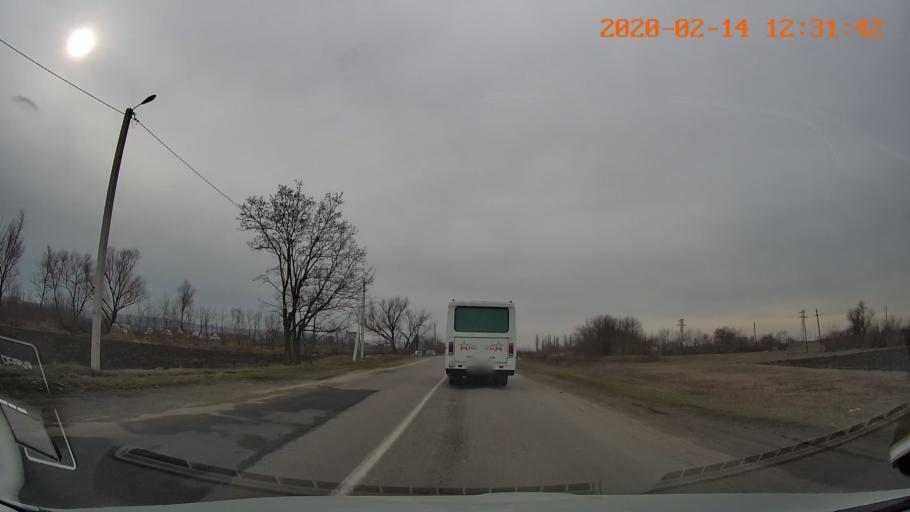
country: RO
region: Botosani
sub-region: Comuna Darabani
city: Bajura
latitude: 48.2472
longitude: 26.5558
